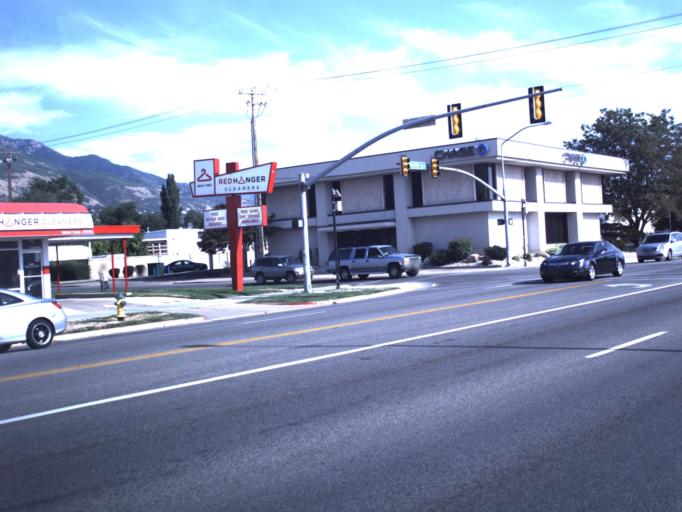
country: US
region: Utah
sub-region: Weber County
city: Ogden
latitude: 41.2127
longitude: -111.9708
